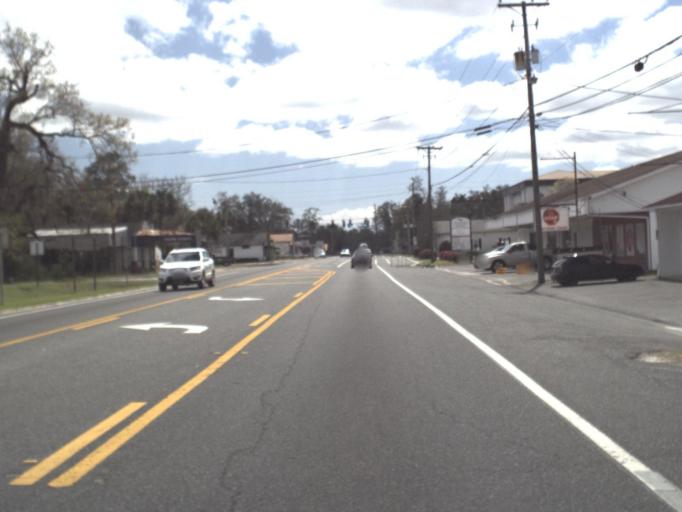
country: US
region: Florida
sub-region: Wakulla County
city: Crawfordville
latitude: 30.1778
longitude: -84.3751
